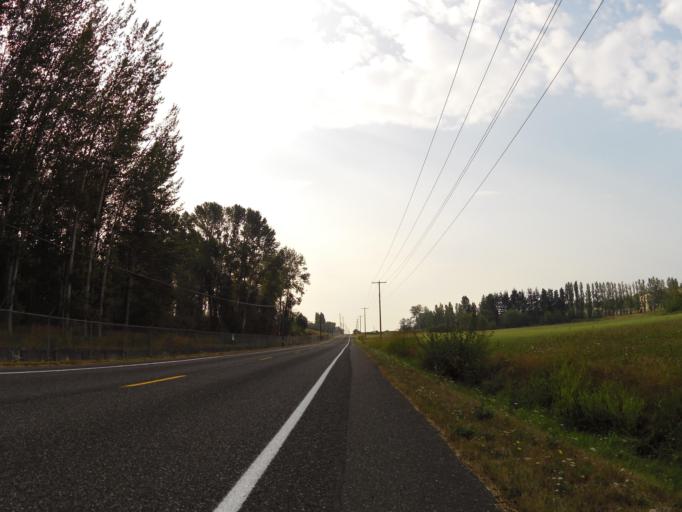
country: US
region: Washington
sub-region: Whatcom County
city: Birch Bay
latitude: 48.8898
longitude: -122.7489
